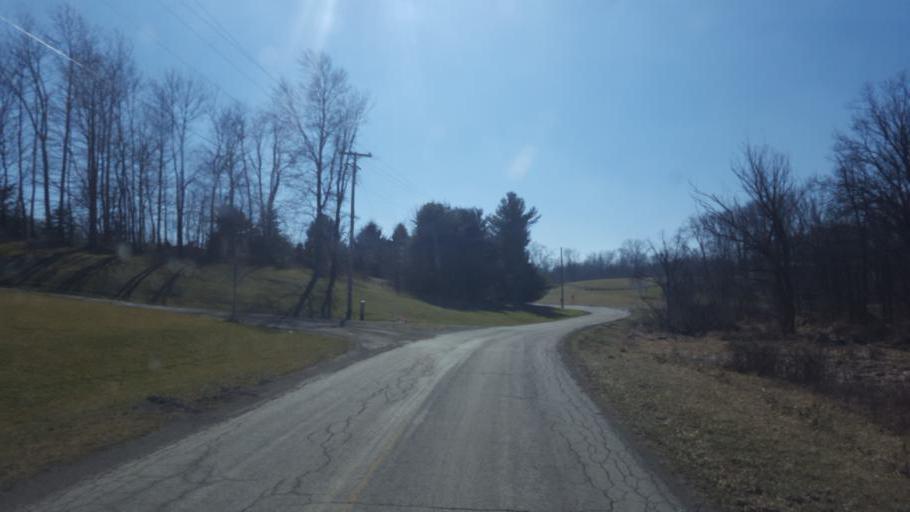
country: US
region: Ohio
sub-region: Richland County
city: Lincoln Heights
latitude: 40.8625
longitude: -82.4825
